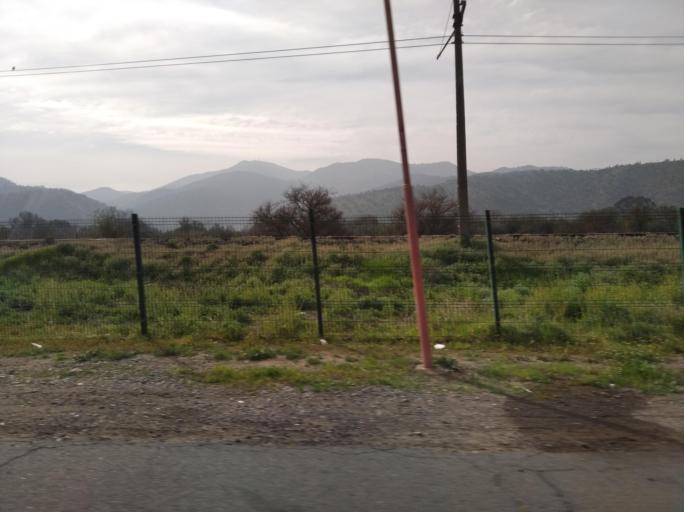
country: CL
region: Santiago Metropolitan
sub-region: Provincia de Chacabuco
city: Lampa
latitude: -33.1146
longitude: -70.9270
